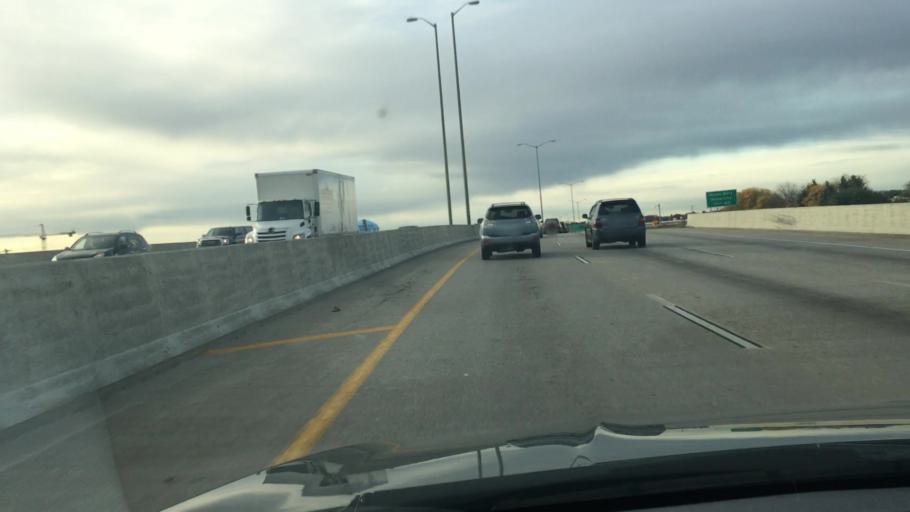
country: US
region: Wisconsin
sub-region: Waukesha County
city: Butler
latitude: 43.0829
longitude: -88.0572
